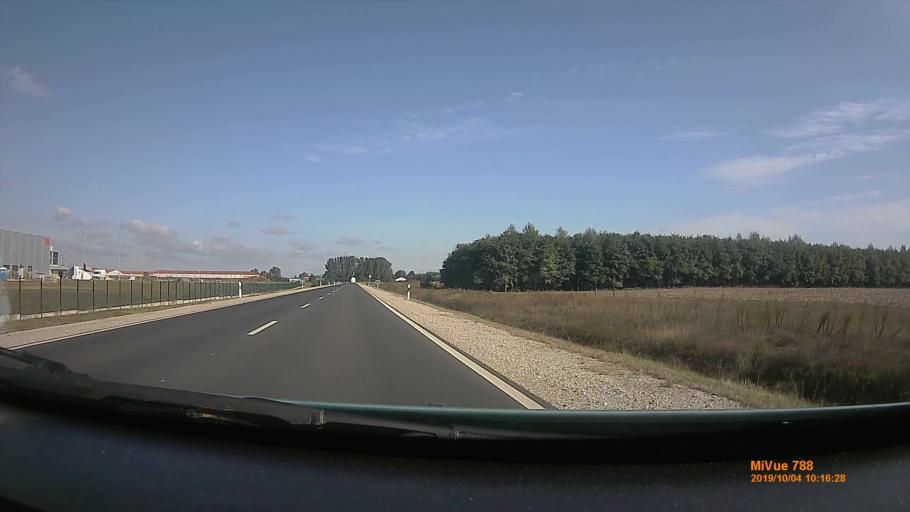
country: HU
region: Szabolcs-Szatmar-Bereg
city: Nyiregyhaza
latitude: 47.9493
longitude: 21.6536
